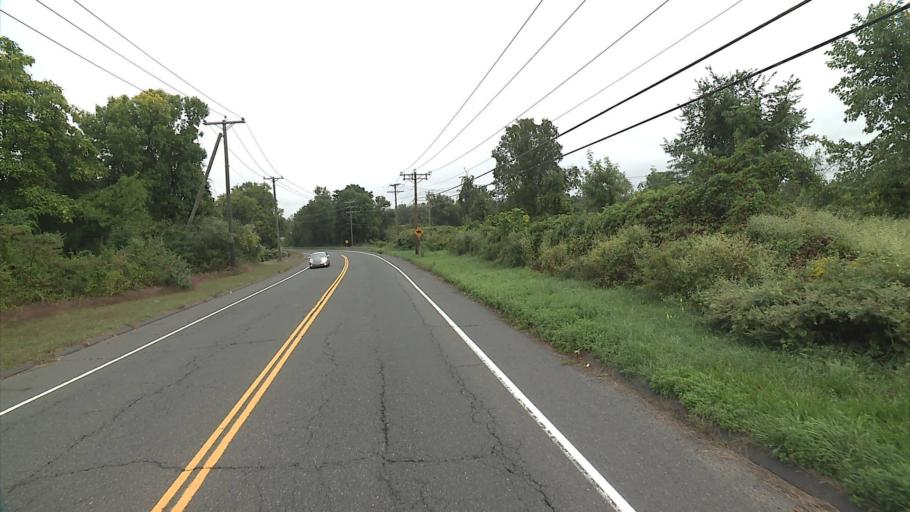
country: US
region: Connecticut
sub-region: Hartford County
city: Windsor Locks
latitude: 41.9382
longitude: -72.6140
